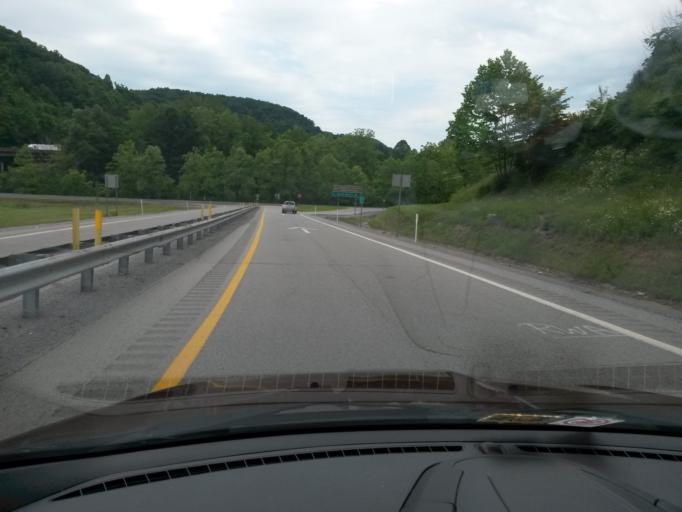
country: US
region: West Virginia
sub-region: Lewis County
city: Weston
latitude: 39.0160
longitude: -80.4702
